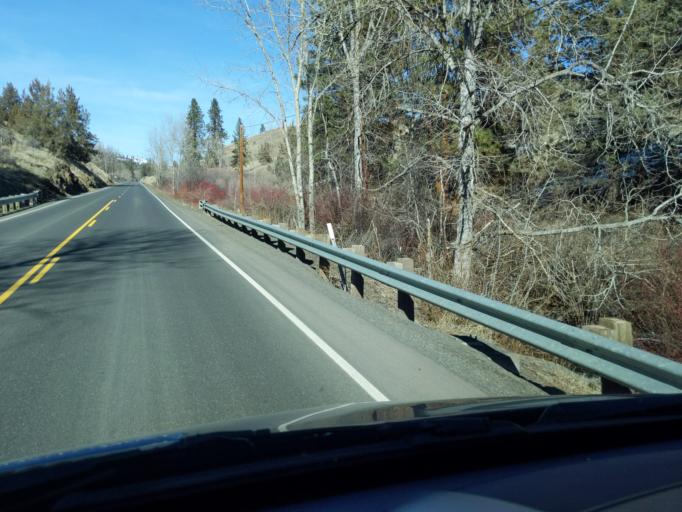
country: US
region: Oregon
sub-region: Grant County
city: John Day
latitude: 44.8463
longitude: -119.0317
